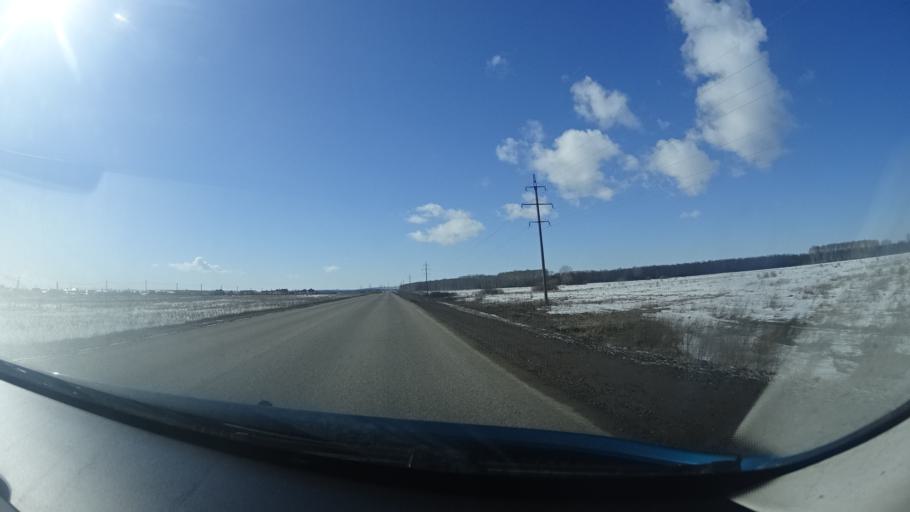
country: RU
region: Bashkortostan
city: Ufa
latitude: 54.6327
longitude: 55.9070
